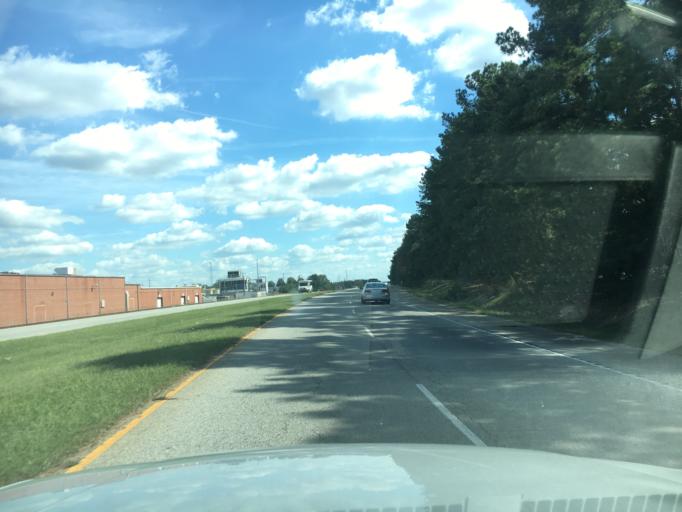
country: US
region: South Carolina
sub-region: Greenville County
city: Mauldin
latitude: 34.7724
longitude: -82.3021
